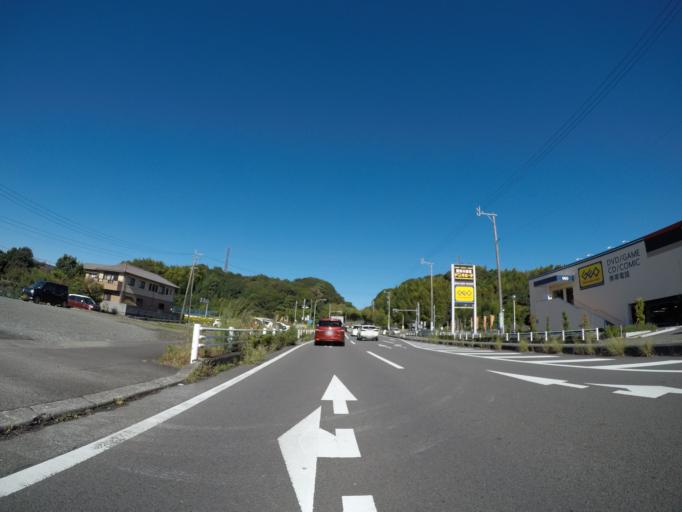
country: JP
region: Shizuoka
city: Fujieda
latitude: 34.8563
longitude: 138.2421
